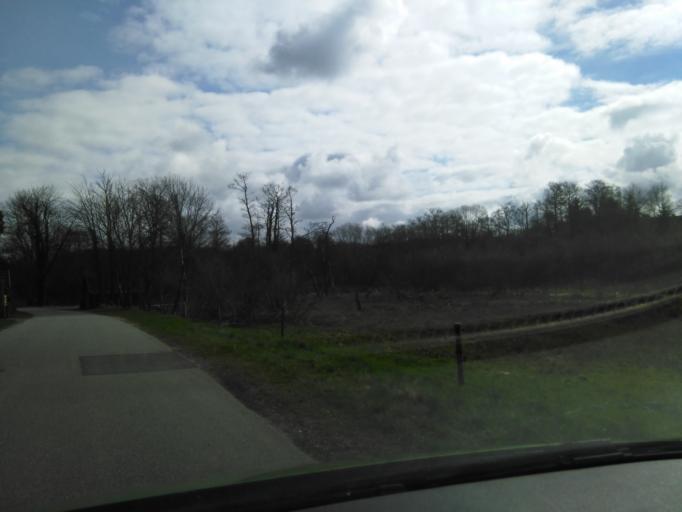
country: DK
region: South Denmark
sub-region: Middelfart Kommune
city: Strib
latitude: 55.5423
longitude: 9.7826
